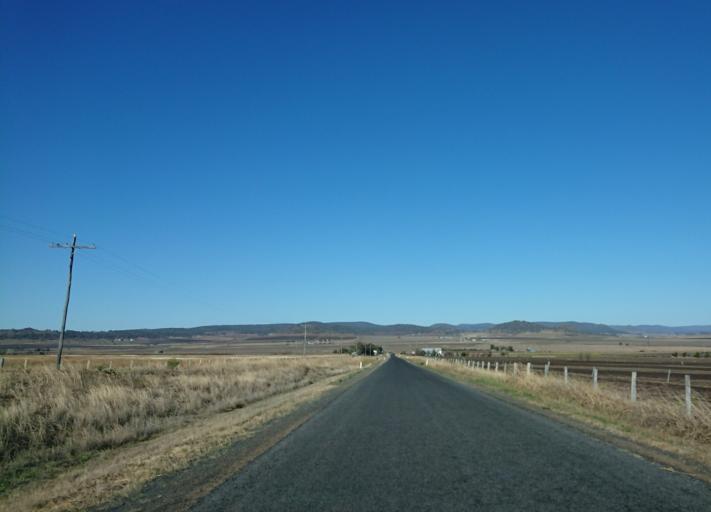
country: AU
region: Queensland
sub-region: Toowoomba
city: Top Camp
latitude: -27.8119
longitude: 151.9743
